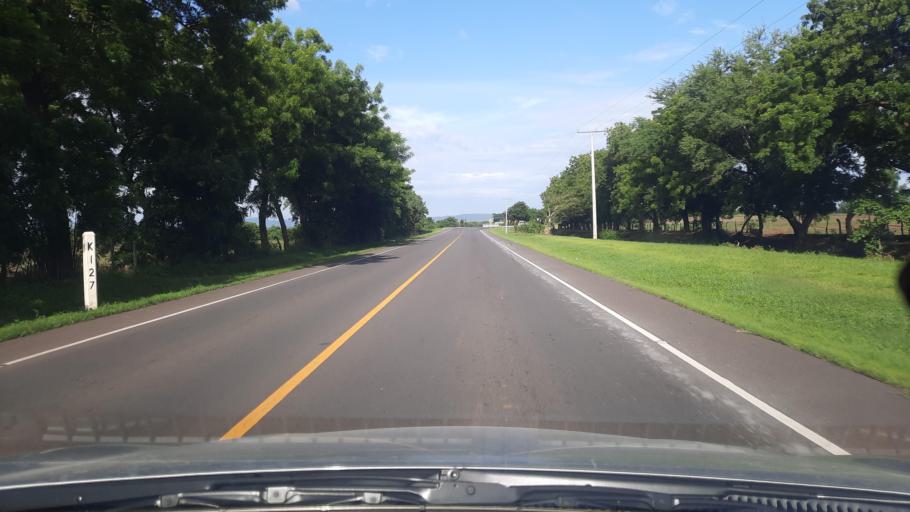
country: NI
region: Chinandega
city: Chichigalpa
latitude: 12.7666
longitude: -86.9076
